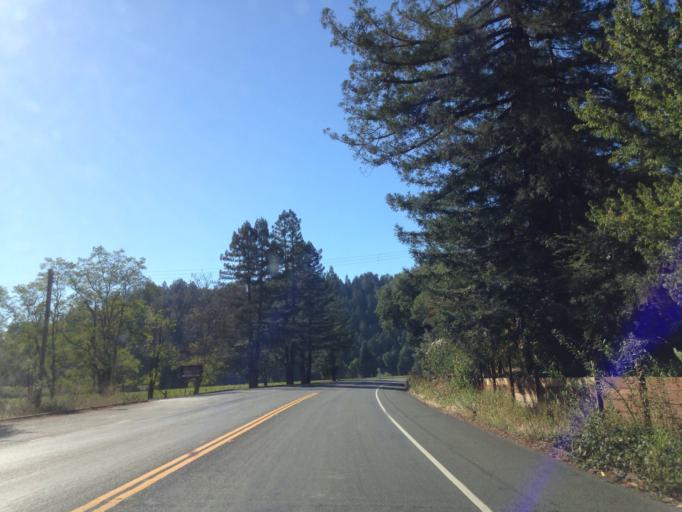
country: US
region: California
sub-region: Sonoma County
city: Guerneville
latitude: 38.5059
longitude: -122.9610
